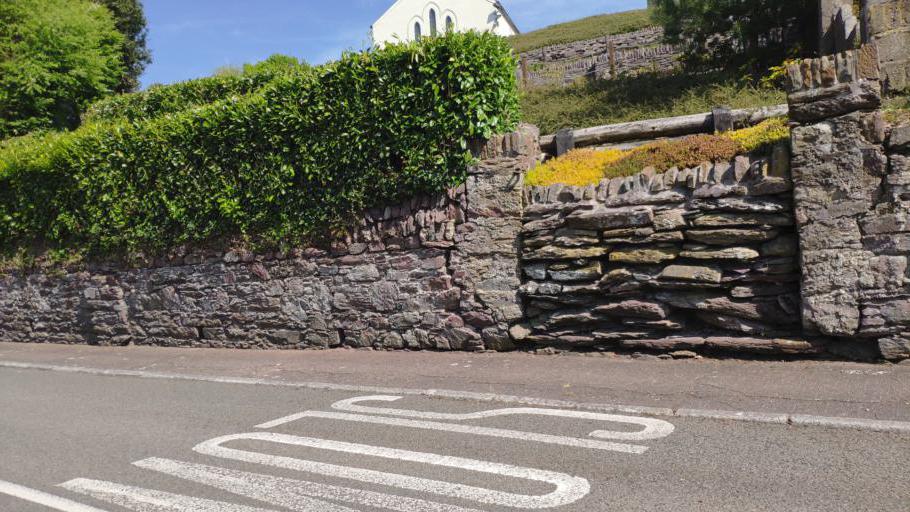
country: IE
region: Munster
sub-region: County Cork
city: Blarney
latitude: 51.9545
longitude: -8.5744
